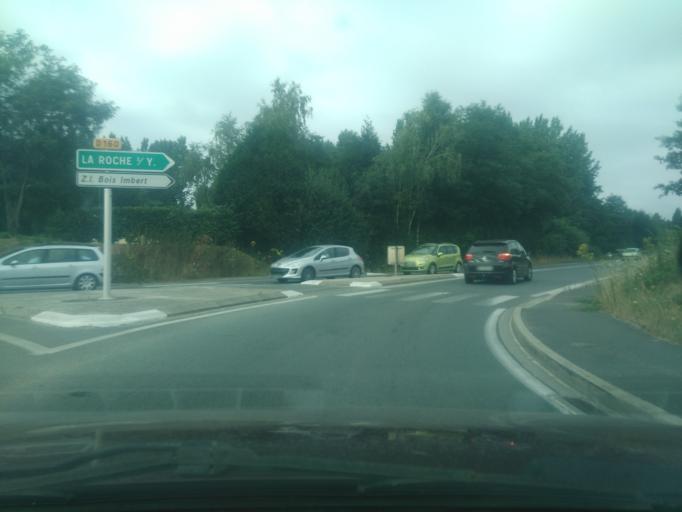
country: FR
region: Pays de la Loire
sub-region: Departement de la Vendee
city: La Ferriere
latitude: 46.7081
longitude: -1.3254
